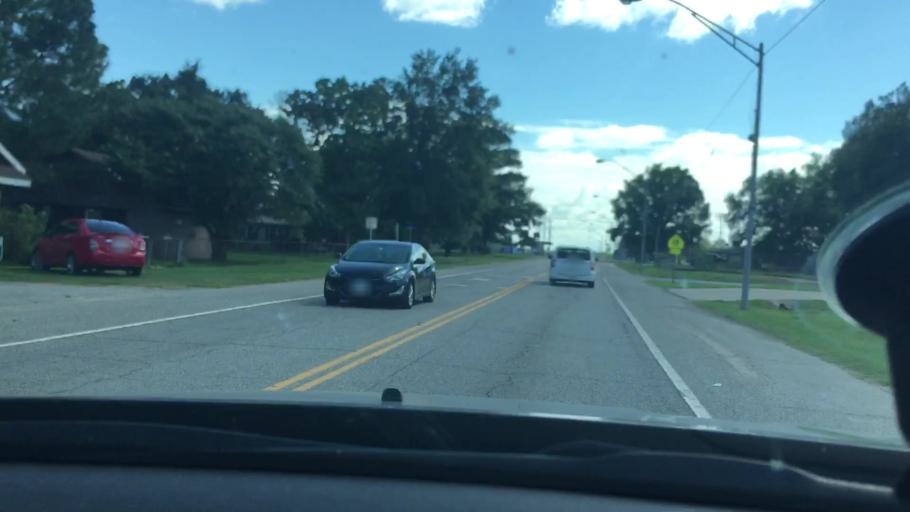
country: US
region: Oklahoma
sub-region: Sequoyah County
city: Vian
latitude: 35.4966
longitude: -94.9702
